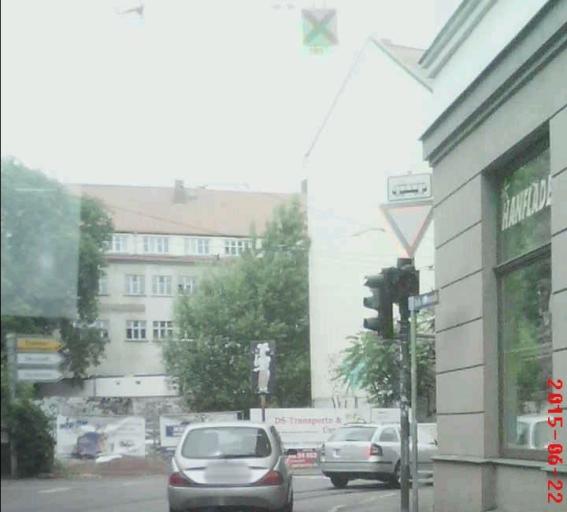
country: DE
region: Saxony-Anhalt
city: Sennewitz
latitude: 51.5007
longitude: 11.9557
